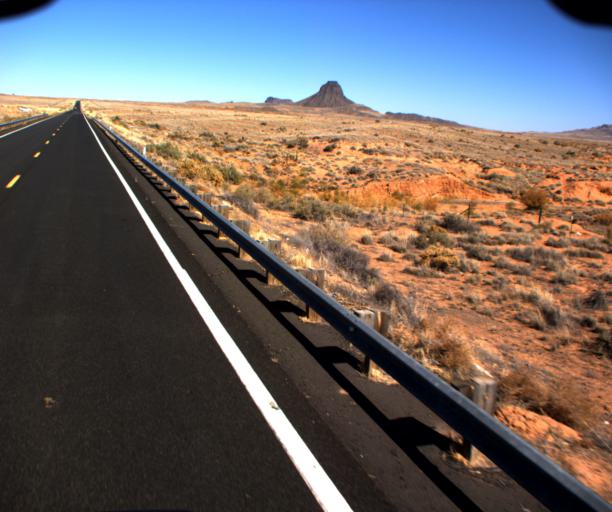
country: US
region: Arizona
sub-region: Navajo County
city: Dilkon
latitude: 35.2644
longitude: -110.4295
